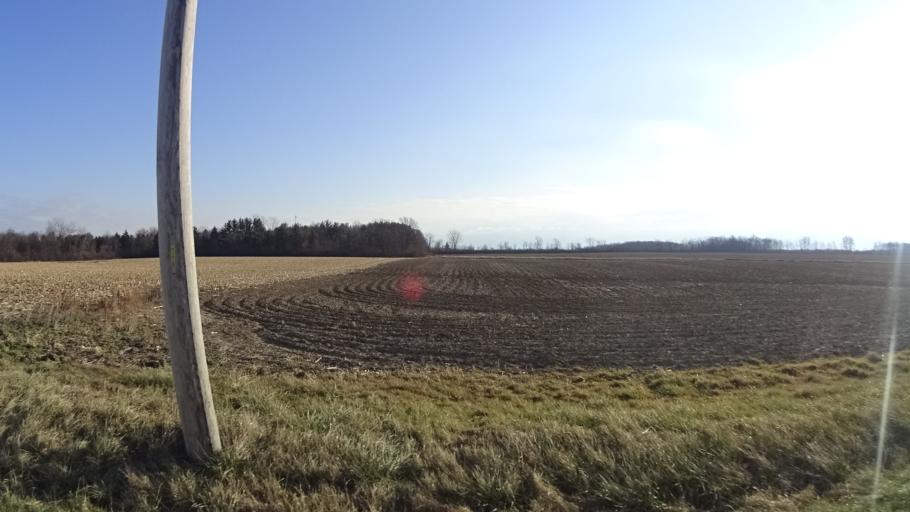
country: US
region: Ohio
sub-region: Lorain County
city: Oberlin
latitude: 41.2605
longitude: -82.2561
